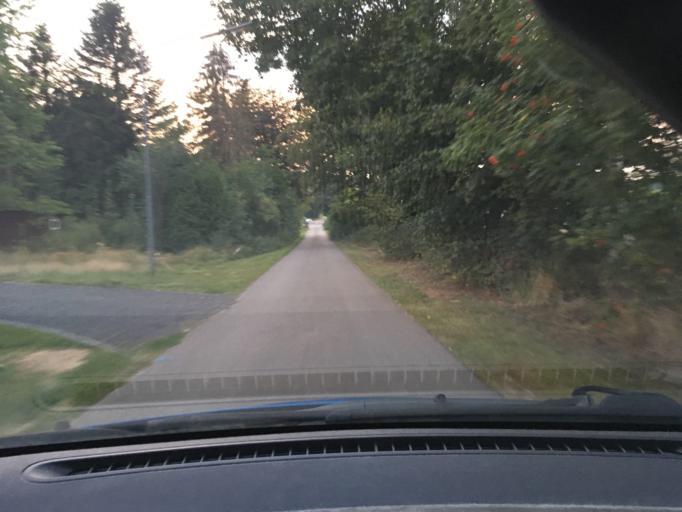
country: DE
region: Lower Saxony
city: Thomasburg
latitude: 53.1881
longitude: 10.6275
